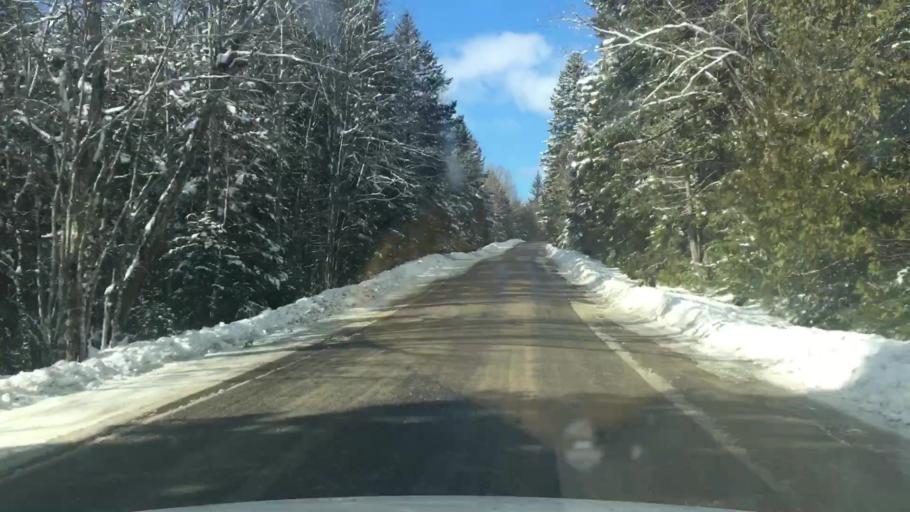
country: US
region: Maine
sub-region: Washington County
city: Machias
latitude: 44.6844
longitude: -67.4584
